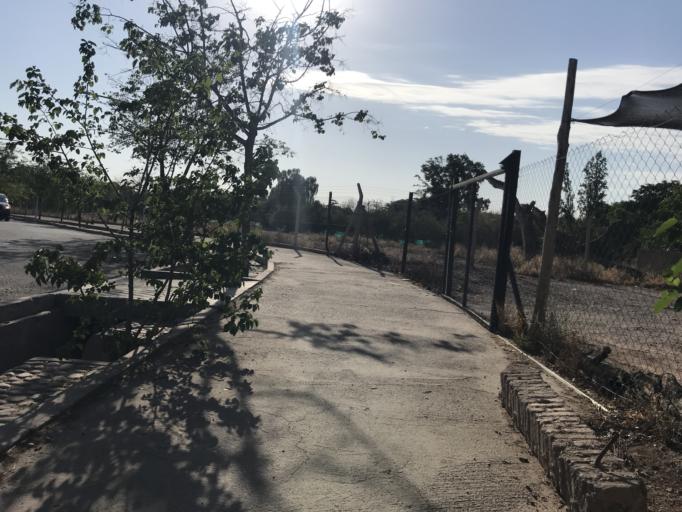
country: AR
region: Mendoza
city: Mendoza
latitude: -32.8791
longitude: -68.8405
